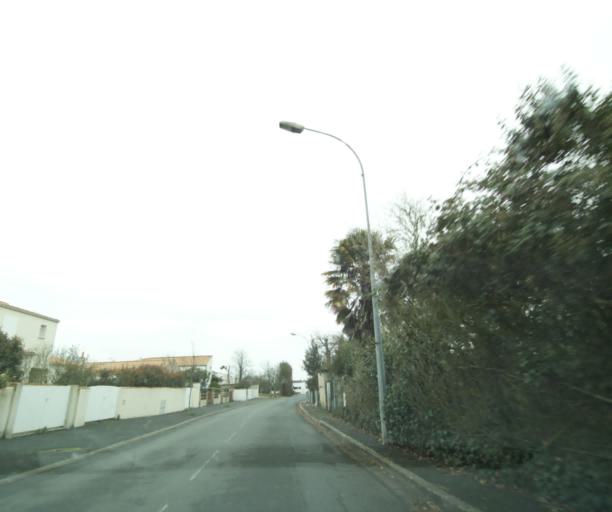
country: FR
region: Poitou-Charentes
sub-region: Departement de la Charente-Maritime
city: Lagord
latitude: 46.1878
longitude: -1.1403
